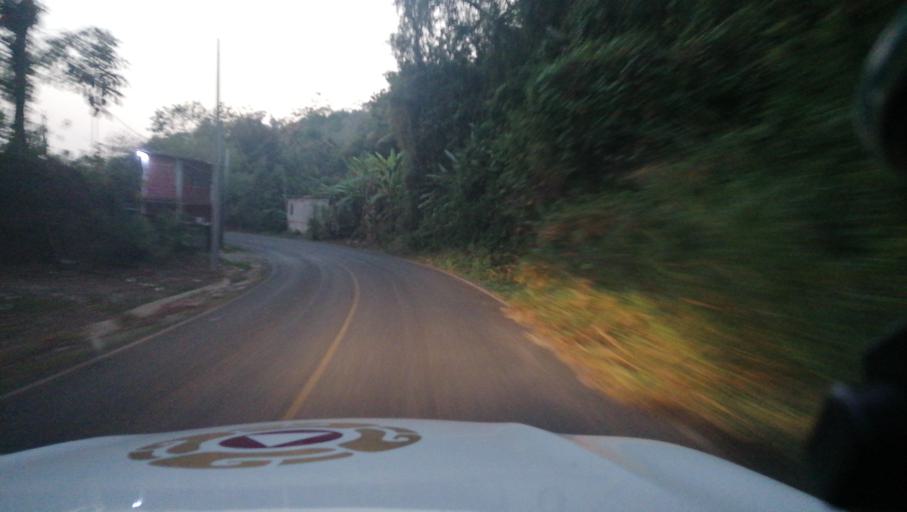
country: MX
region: Chiapas
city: Veinte de Noviembre
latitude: 14.9931
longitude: -92.2440
